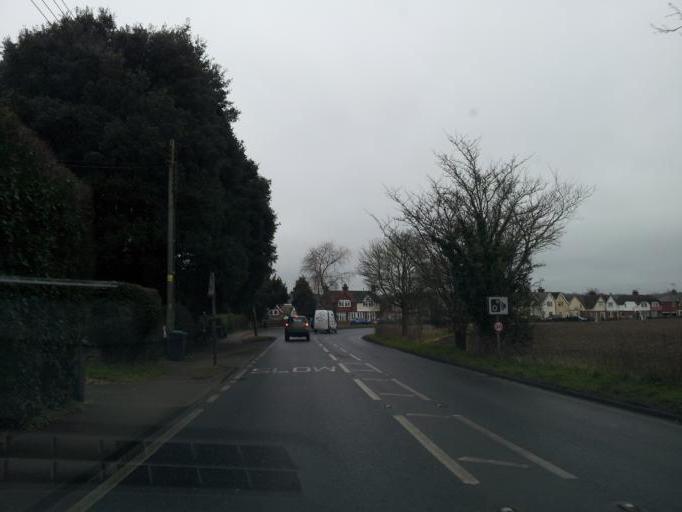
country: GB
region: England
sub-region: Essex
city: Manningtree
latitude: 51.9609
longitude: 1.0614
